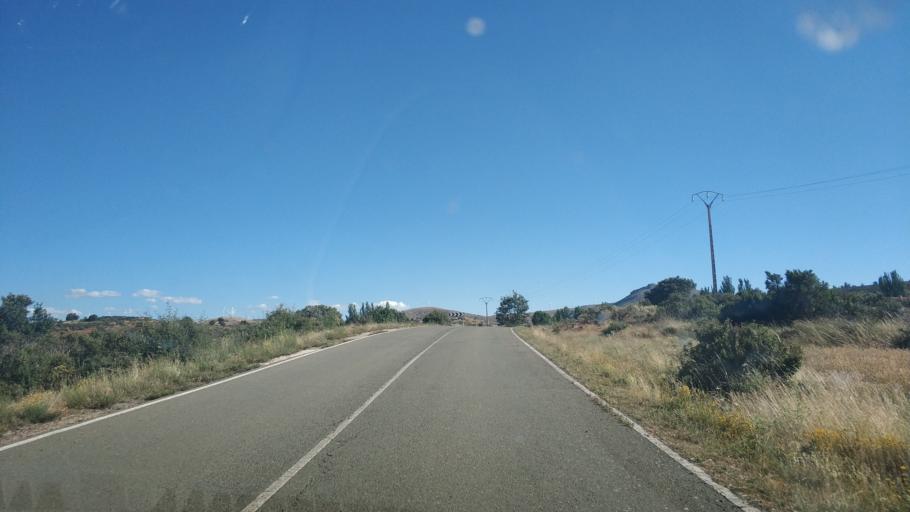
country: ES
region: Castille and Leon
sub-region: Provincia de Soria
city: Montejo de Tiermes
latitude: 41.3389
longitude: -3.1511
